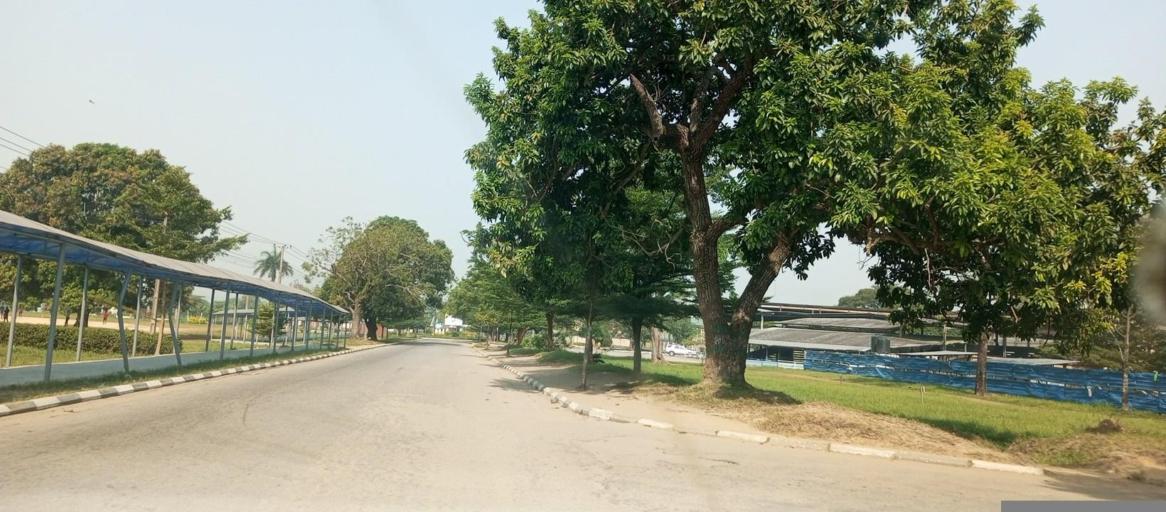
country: NG
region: Rivers
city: Emuoha
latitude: 4.9018
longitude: 6.9223
